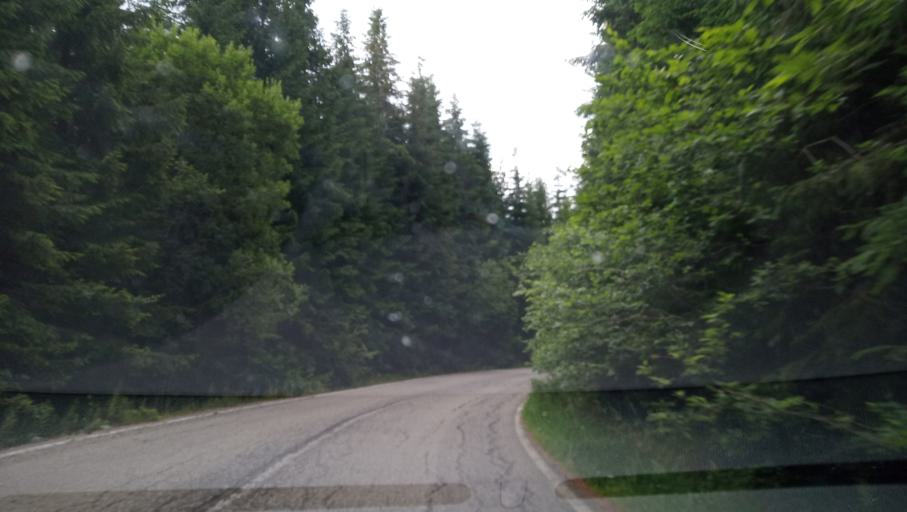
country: RO
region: Valcea
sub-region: Comuna Voineasa
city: Voineasa
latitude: 45.4228
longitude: 23.7571
